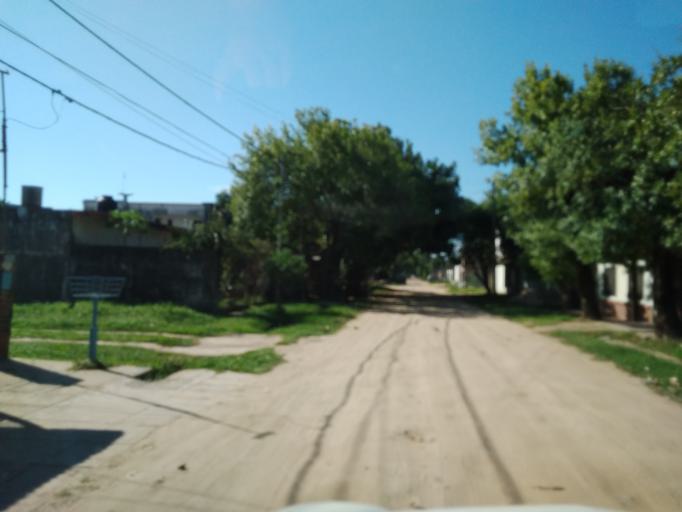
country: AR
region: Corrientes
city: Corrientes
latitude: -27.4852
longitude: -58.8049
